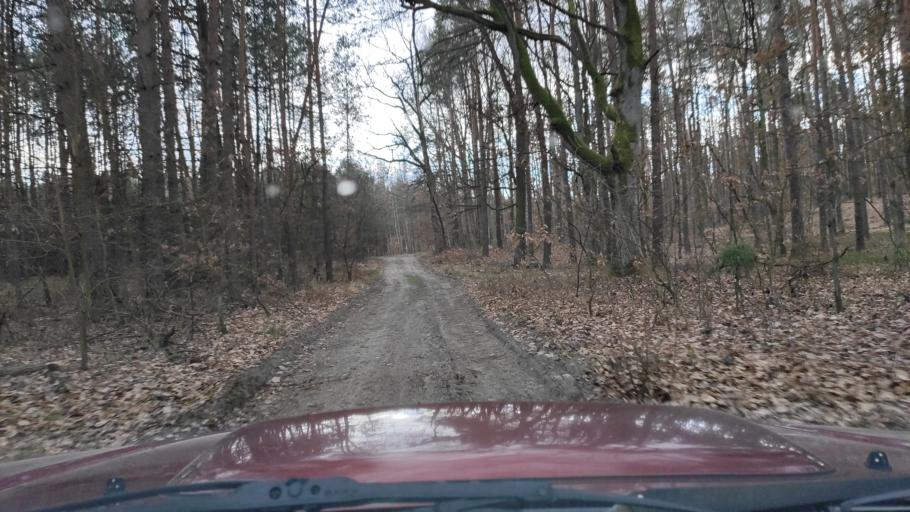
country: PL
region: Masovian Voivodeship
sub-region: Powiat kozienicki
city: Garbatka-Letnisko
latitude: 51.5096
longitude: 21.5620
